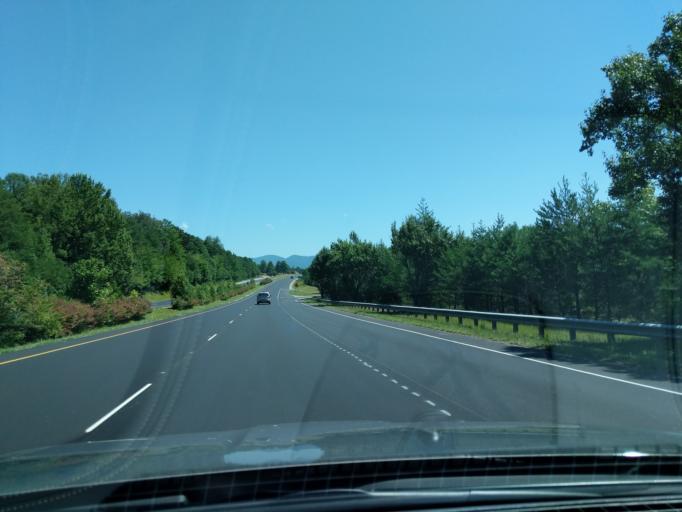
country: US
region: North Carolina
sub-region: Macon County
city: Franklin
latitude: 35.1666
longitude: -83.4020
